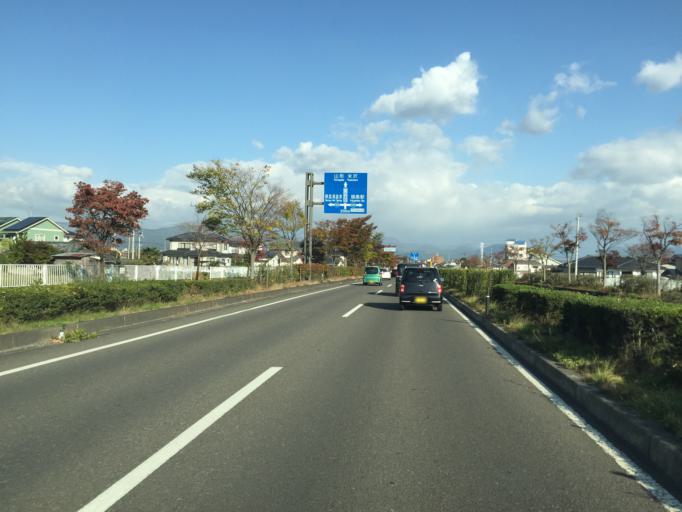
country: JP
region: Fukushima
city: Fukushima-shi
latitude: 37.7469
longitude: 140.4368
